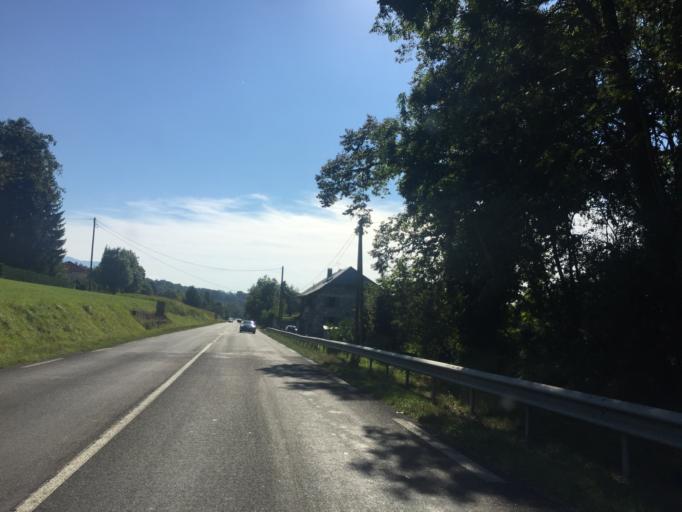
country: FR
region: Rhone-Alpes
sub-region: Departement de la Haute-Savoie
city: Viuz-la-Chiesaz
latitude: 45.8358
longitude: 6.0568
